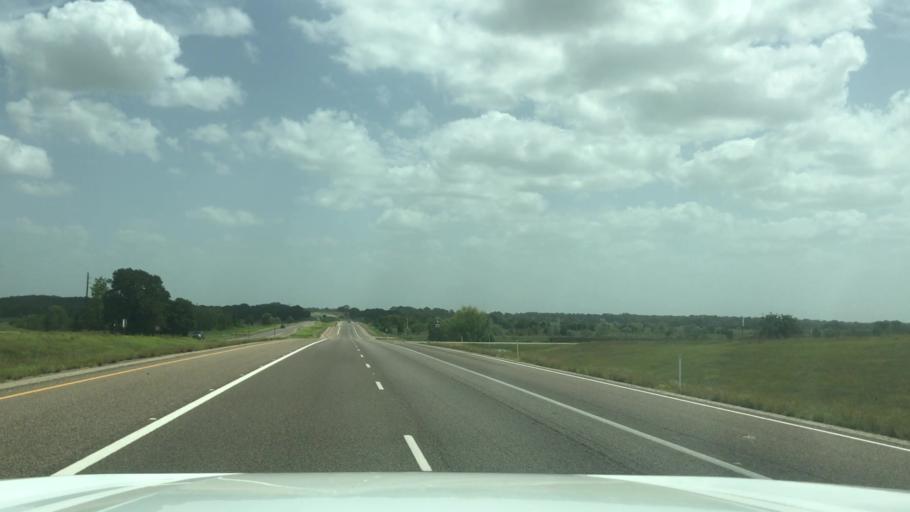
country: US
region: Texas
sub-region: Robertson County
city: Calvert
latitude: 31.0218
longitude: -96.7079
